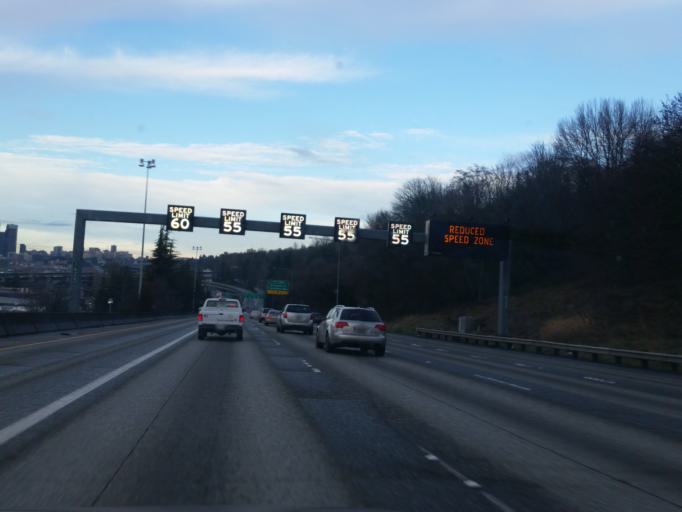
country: US
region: Washington
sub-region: King County
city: Seattle
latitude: 47.5643
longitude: -122.3210
